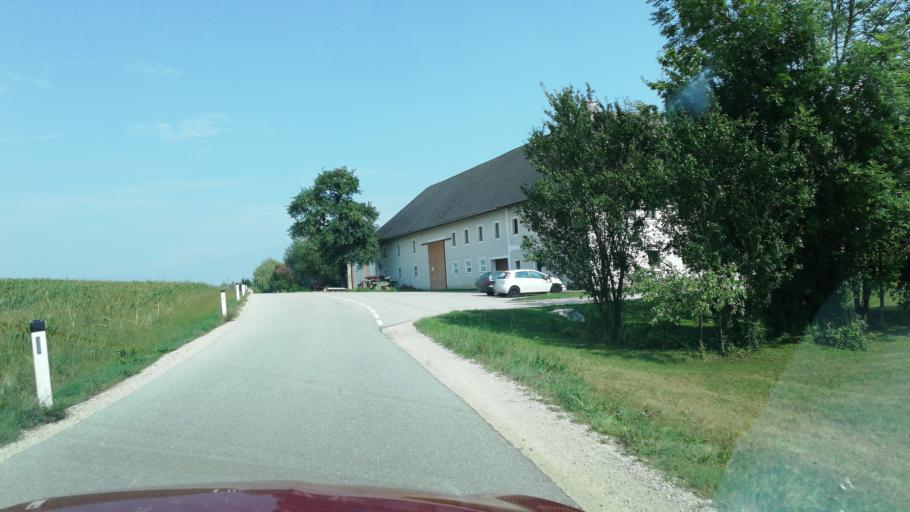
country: AT
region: Upper Austria
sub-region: Politischer Bezirk Steyr-Land
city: Sierning
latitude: 48.0530
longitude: 14.3105
